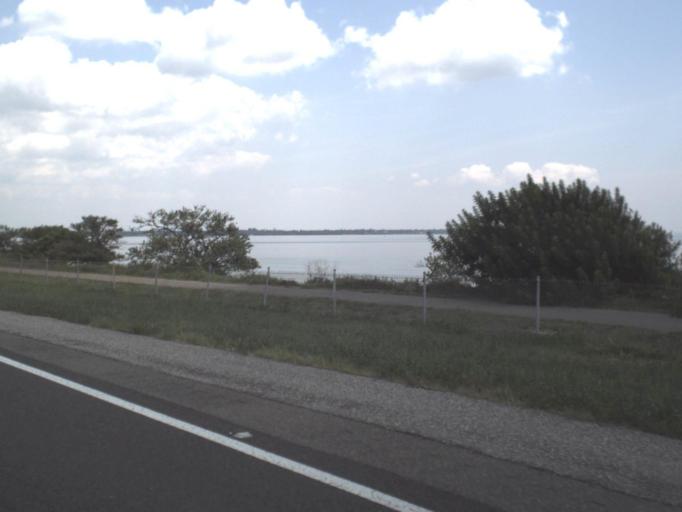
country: US
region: Florida
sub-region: Pinellas County
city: Tierra Verde
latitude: 27.6696
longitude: -82.6776
